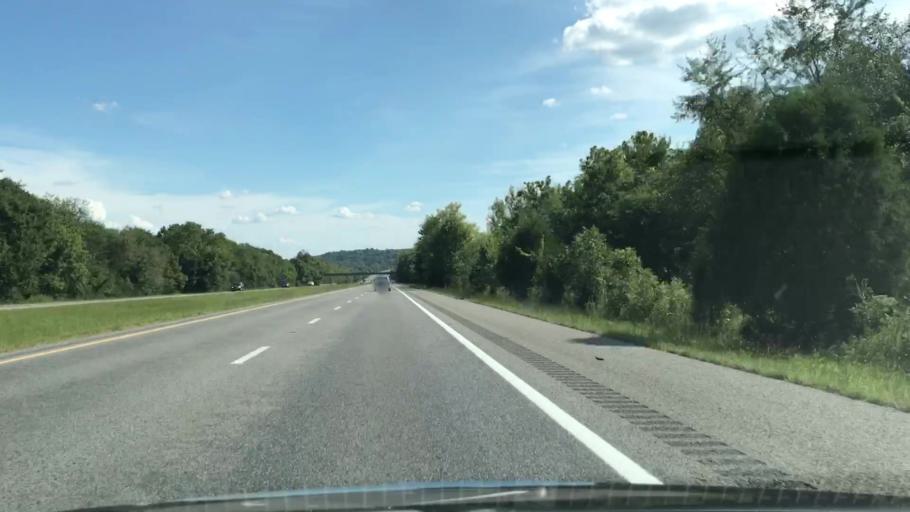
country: US
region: Alabama
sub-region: Limestone County
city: Ardmore
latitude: 35.1432
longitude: -86.8787
